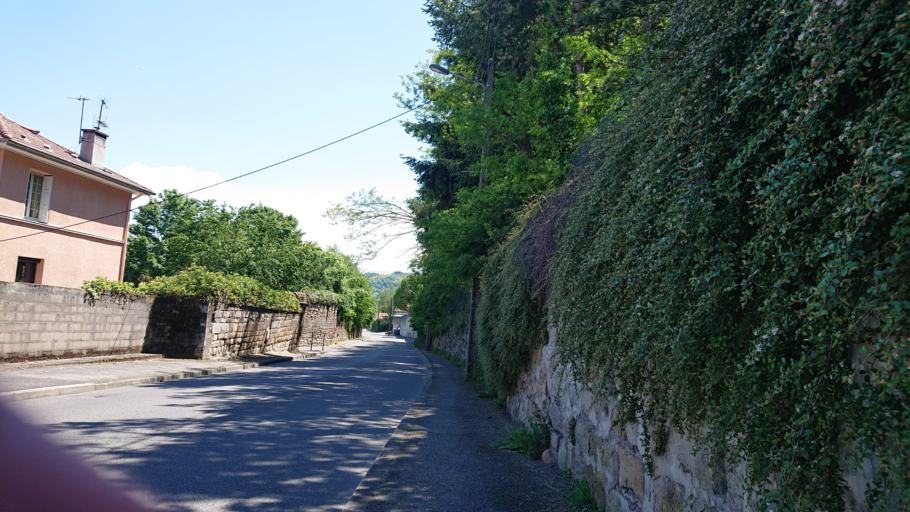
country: FR
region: Rhone-Alpes
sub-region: Departement de la Loire
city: Villars
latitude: 45.4491
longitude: 4.3605
